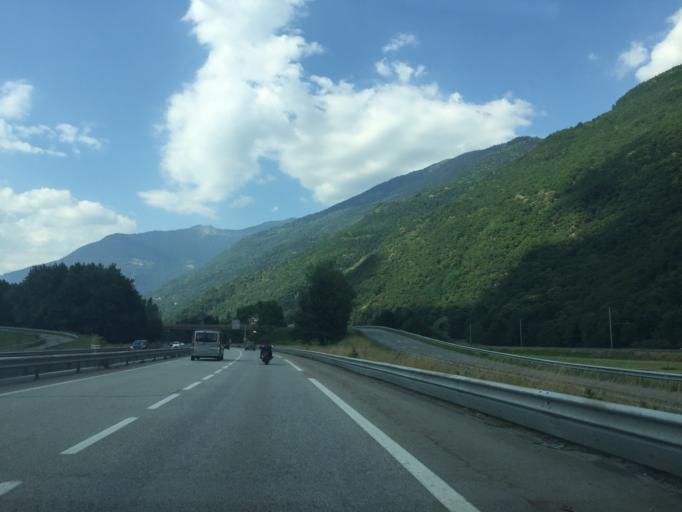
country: FR
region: Rhone-Alpes
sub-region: Departement de la Savoie
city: La Bathie
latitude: 45.6070
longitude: 6.4509
